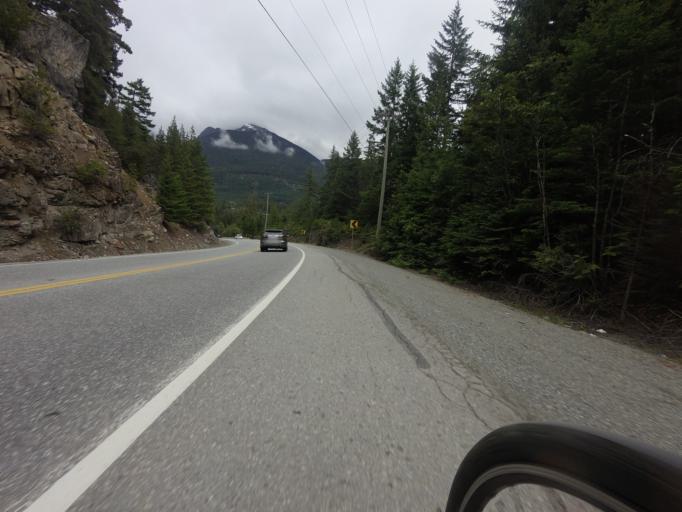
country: CA
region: British Columbia
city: Whistler
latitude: 50.1667
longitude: -122.8985
